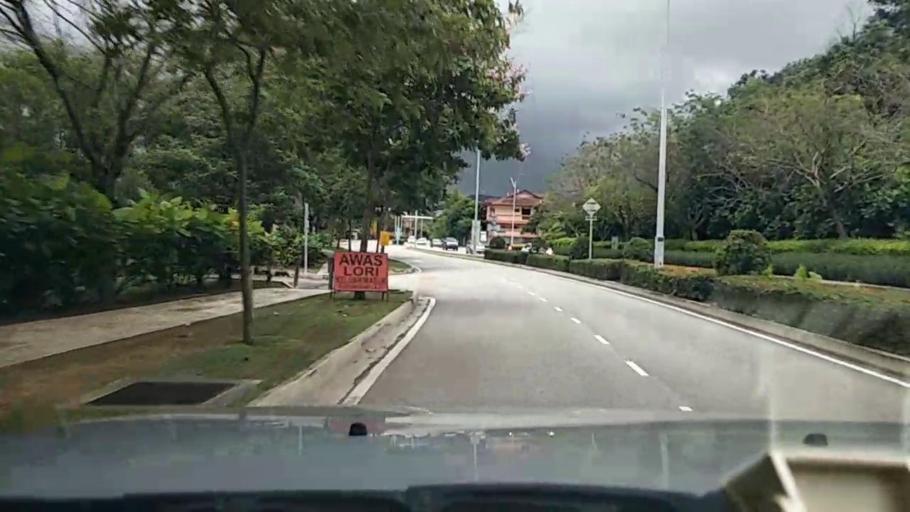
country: MY
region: Putrajaya
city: Putrajaya
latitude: 2.9321
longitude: 101.7018
